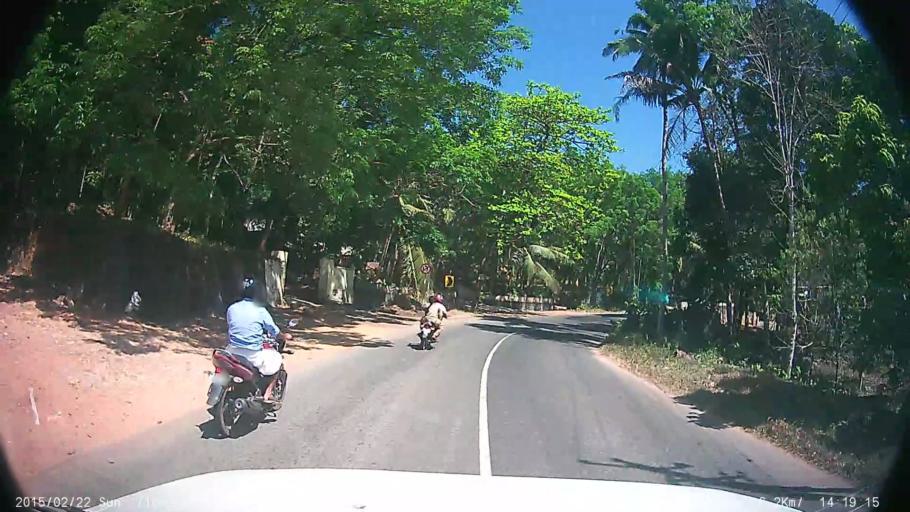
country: IN
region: Kerala
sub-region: Kottayam
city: Lalam
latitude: 9.5674
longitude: 76.6904
